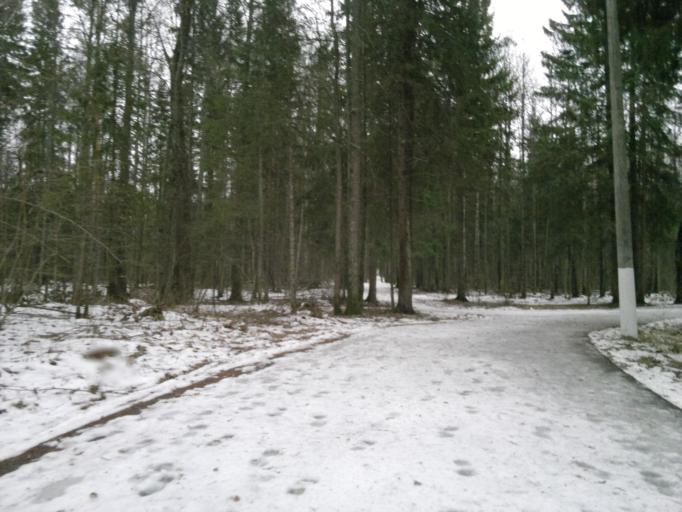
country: RU
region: Mariy-El
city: Yoshkar-Ola
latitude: 56.6020
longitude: 47.9641
